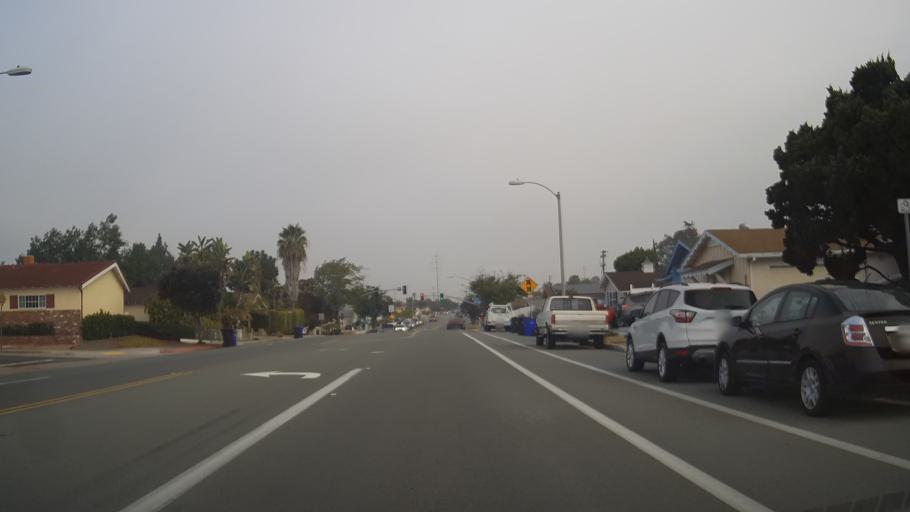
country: US
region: California
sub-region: San Diego County
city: San Diego
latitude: 32.7886
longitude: -117.1448
